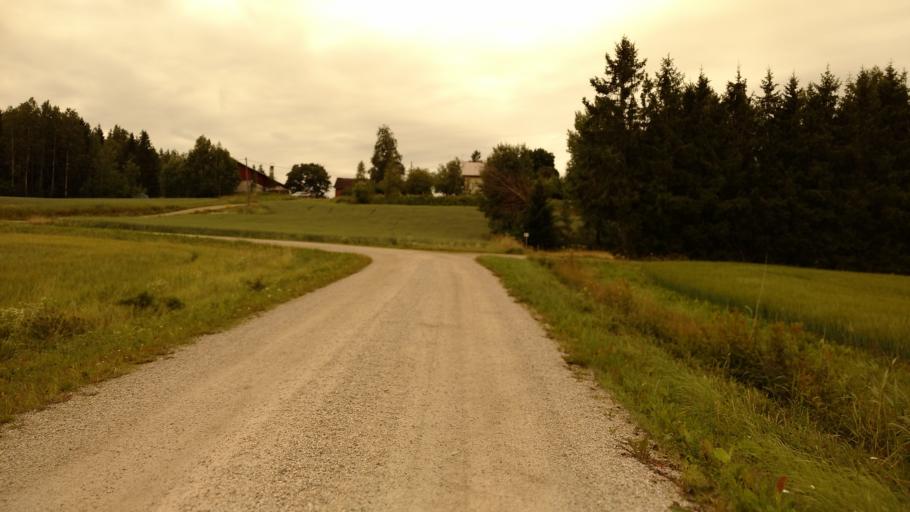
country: FI
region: Varsinais-Suomi
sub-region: Turku
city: Paimio
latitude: 60.4177
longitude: 22.8334
